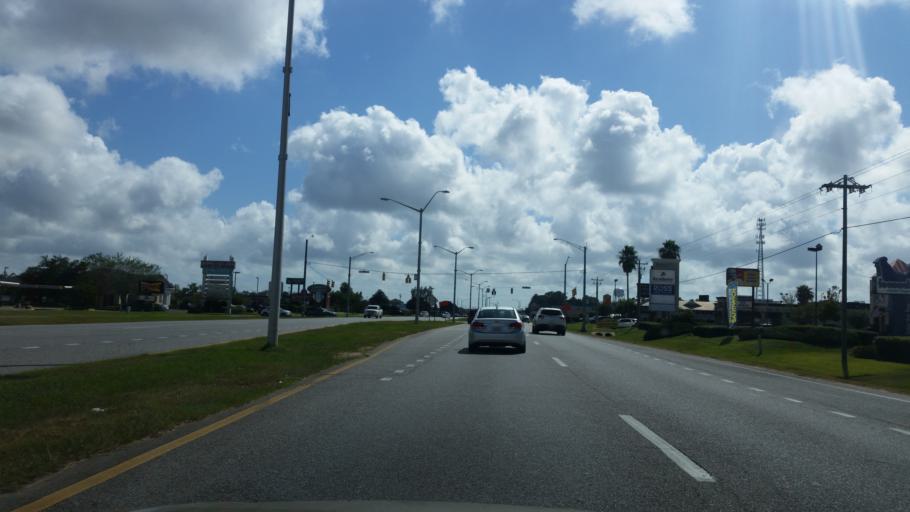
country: US
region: Alabama
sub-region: Baldwin County
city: Foley
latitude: 30.3807
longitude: -87.6833
